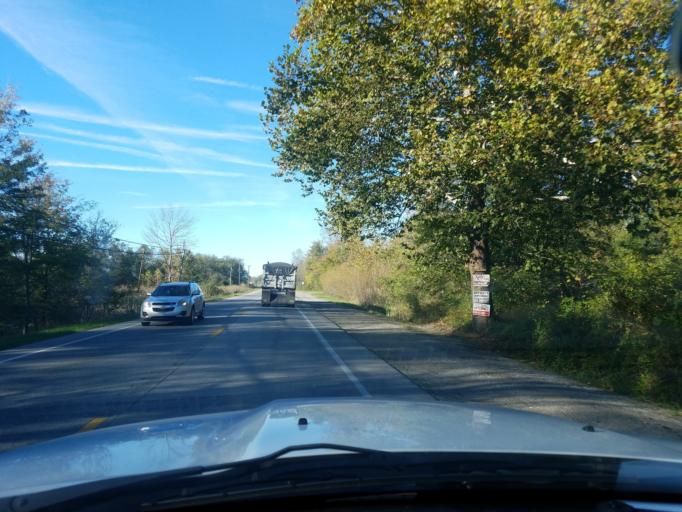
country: US
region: Kentucky
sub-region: Laurel County
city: London
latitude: 37.0769
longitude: -84.0588
